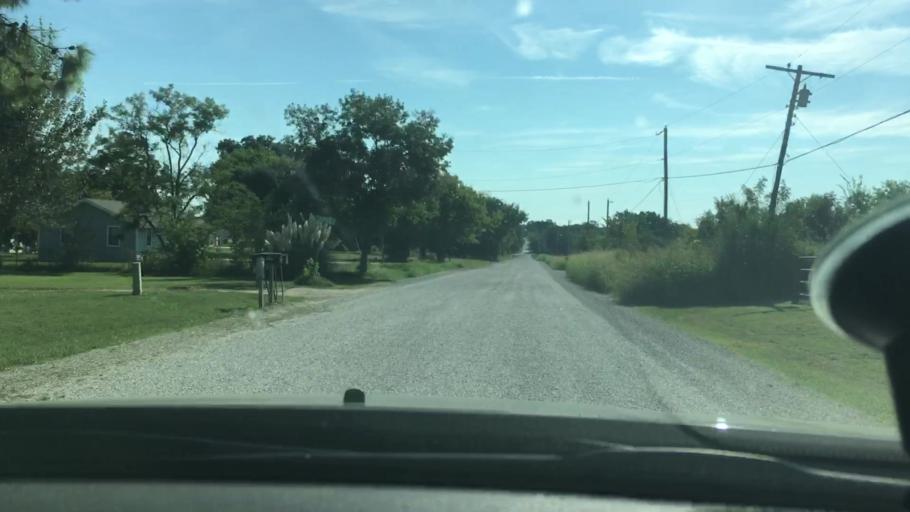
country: US
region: Oklahoma
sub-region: Carter County
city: Lone Grove
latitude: 34.2165
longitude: -97.2533
